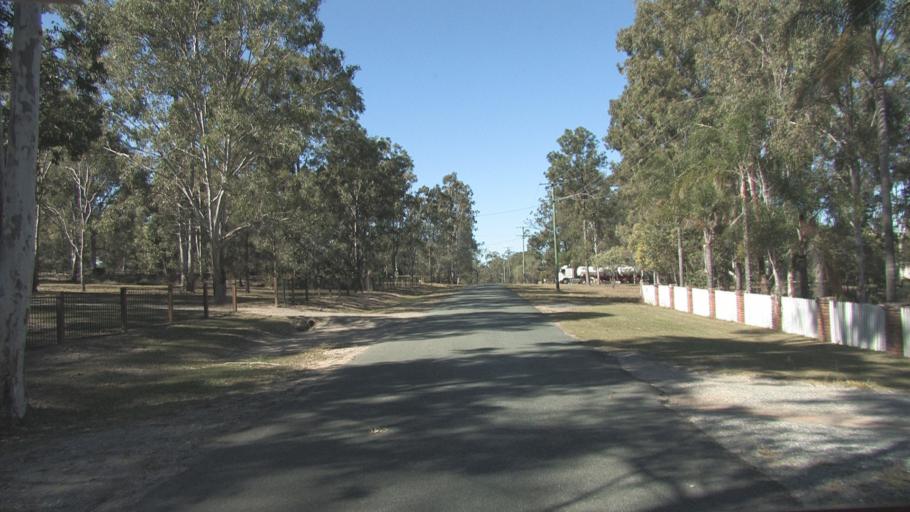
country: AU
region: Queensland
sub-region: Ipswich
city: Springfield Lakes
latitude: -27.7029
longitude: 152.9664
